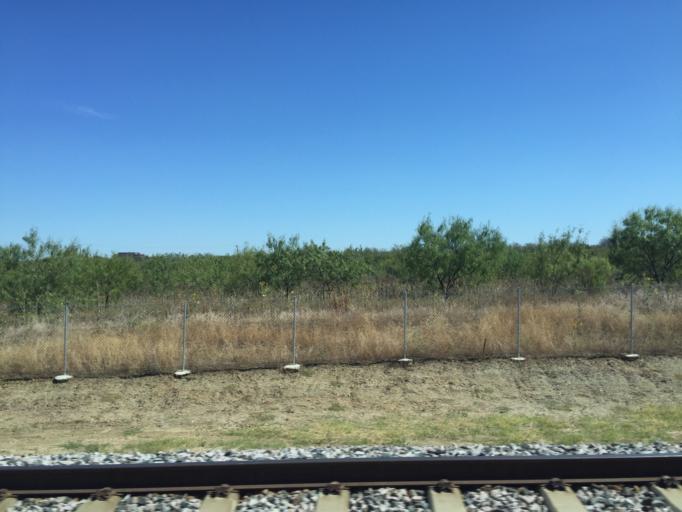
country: US
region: Texas
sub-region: Dallas County
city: Irving
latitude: 32.8789
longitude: -96.9788
